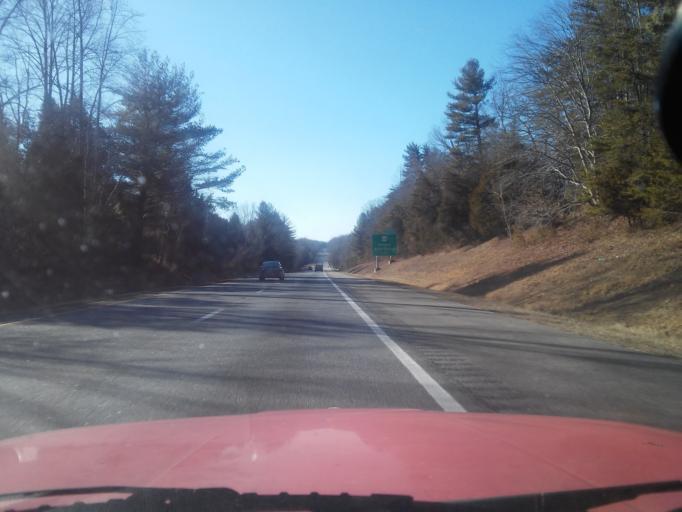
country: US
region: Virginia
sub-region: Fluvanna County
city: Lake Monticello
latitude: 37.9966
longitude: -78.3154
